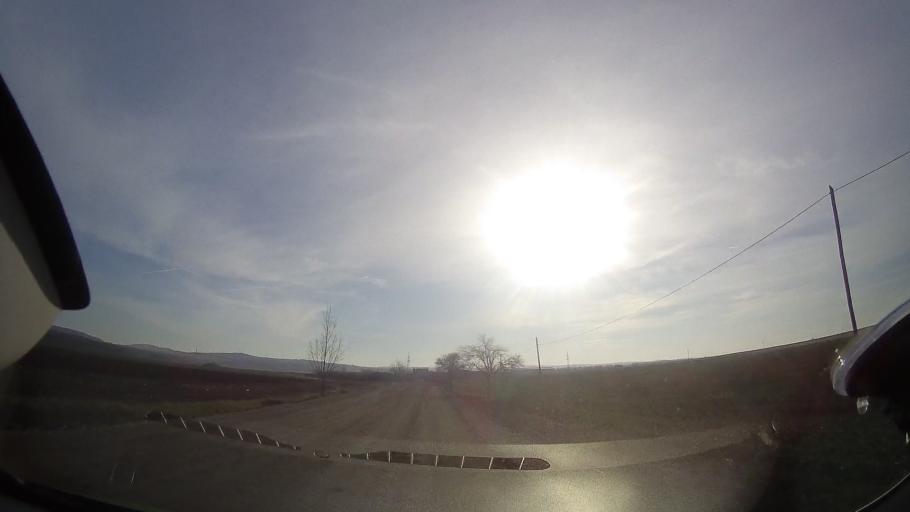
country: RO
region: Bihor
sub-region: Comuna Ciuhoiu
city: Ciuhoiu
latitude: 47.2202
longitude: 22.1343
